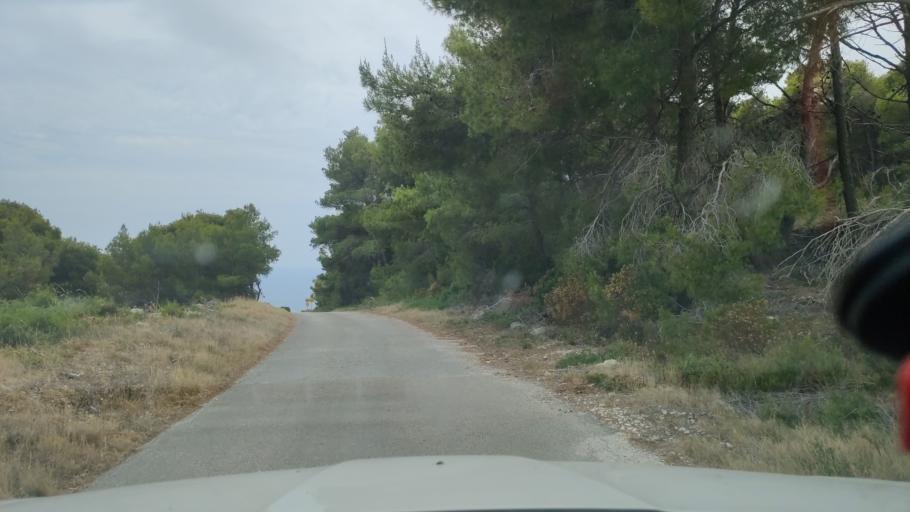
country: HR
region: Splitsko-Dalmatinska
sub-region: Grad Vis
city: Vis
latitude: 43.0272
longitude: 16.1679
